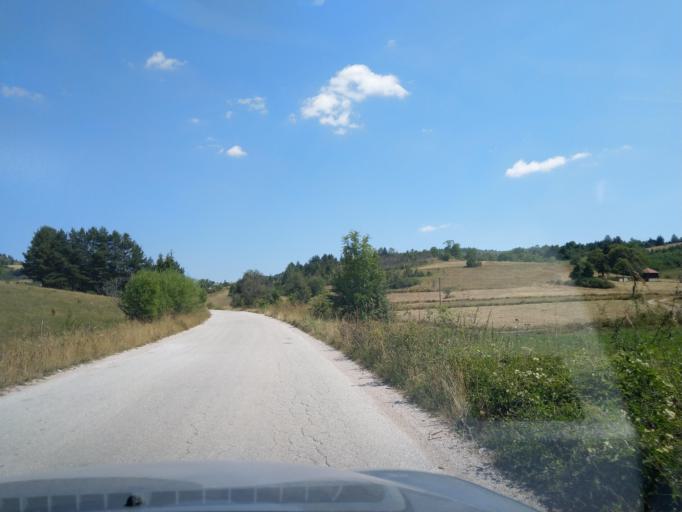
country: RS
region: Central Serbia
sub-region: Zlatiborski Okrug
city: Nova Varos
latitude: 43.4481
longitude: 19.9665
